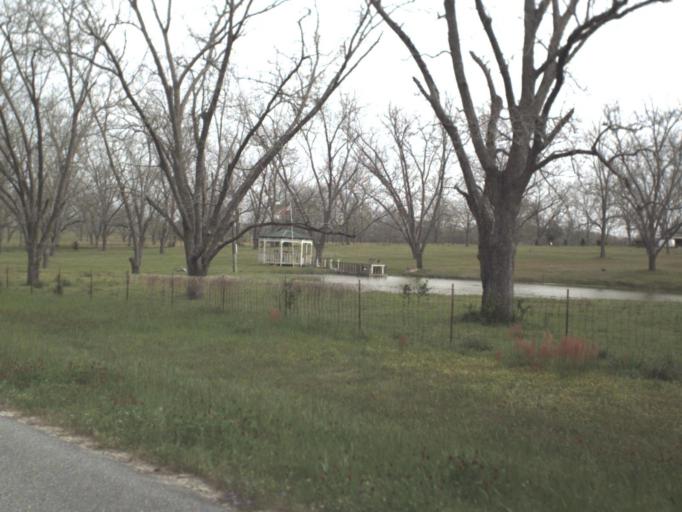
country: US
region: Florida
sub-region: Holmes County
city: Bonifay
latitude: 30.9154
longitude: -85.6495
